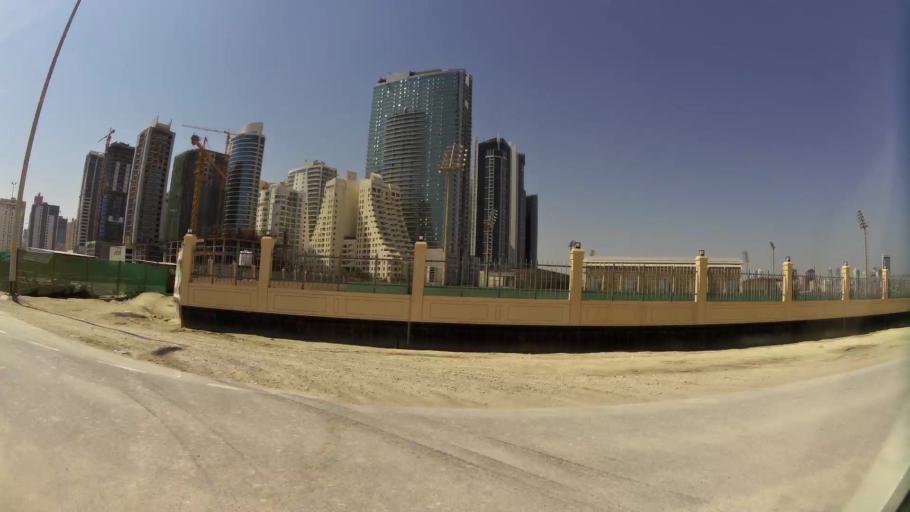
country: BH
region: Manama
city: Manama
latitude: 26.2254
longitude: 50.6121
